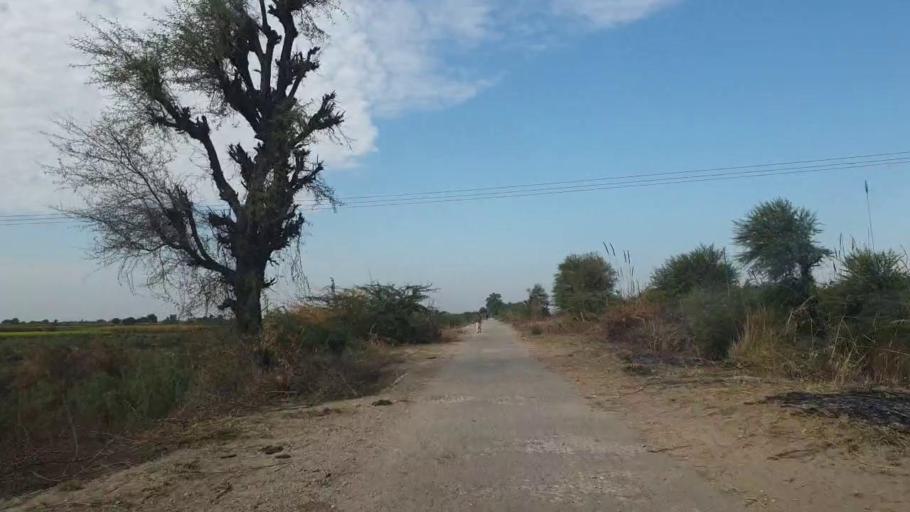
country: PK
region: Sindh
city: Sinjhoro
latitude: 26.0352
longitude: 68.8783
